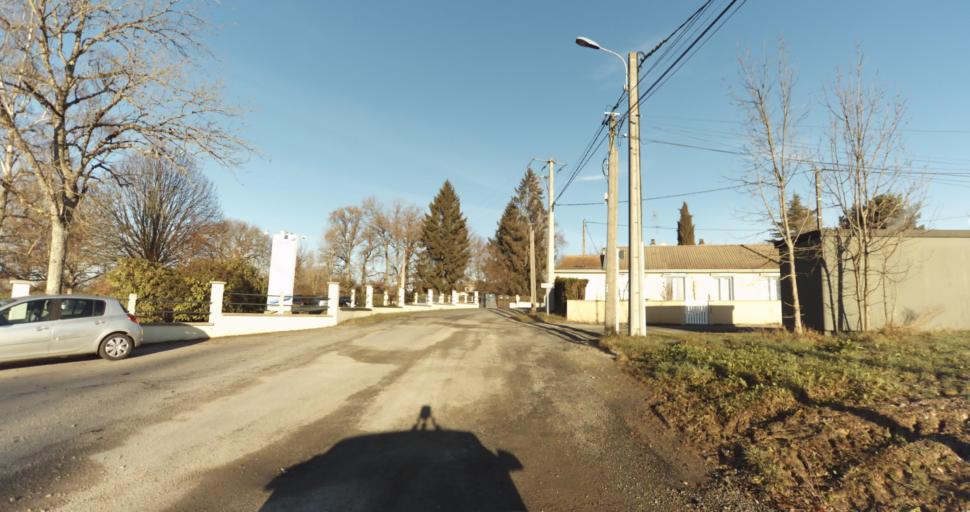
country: FR
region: Limousin
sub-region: Departement de la Haute-Vienne
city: Aixe-sur-Vienne
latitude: 45.8117
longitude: 1.1373
